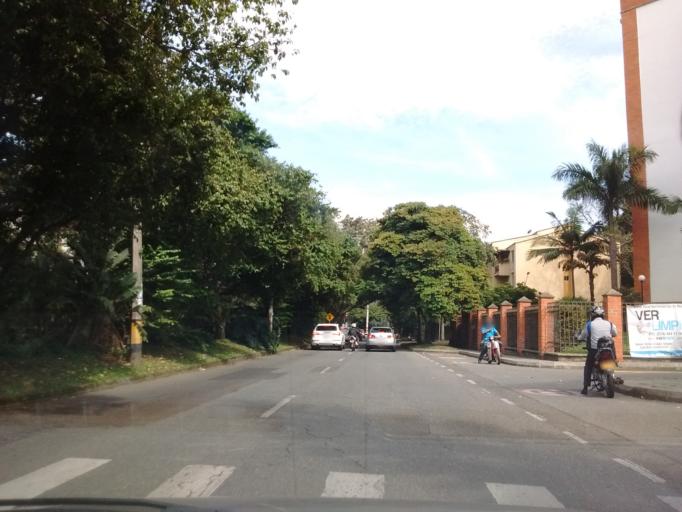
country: CO
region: Antioquia
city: Itagui
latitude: 6.2053
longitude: -75.5759
